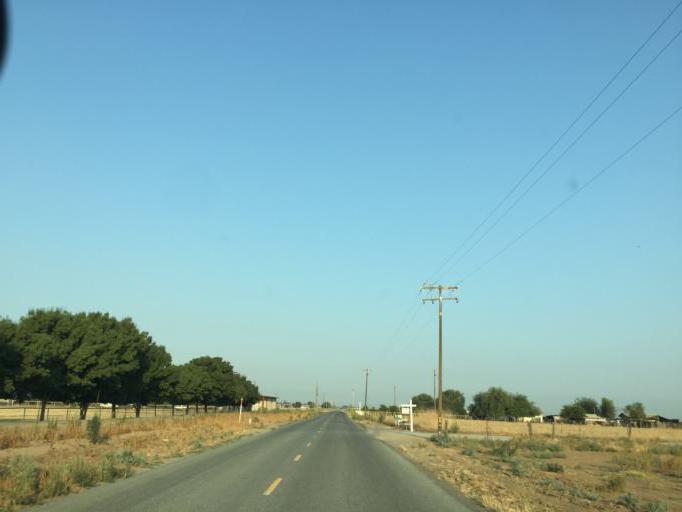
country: US
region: California
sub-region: Tulare County
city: Cutler
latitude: 36.4436
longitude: -119.3468
